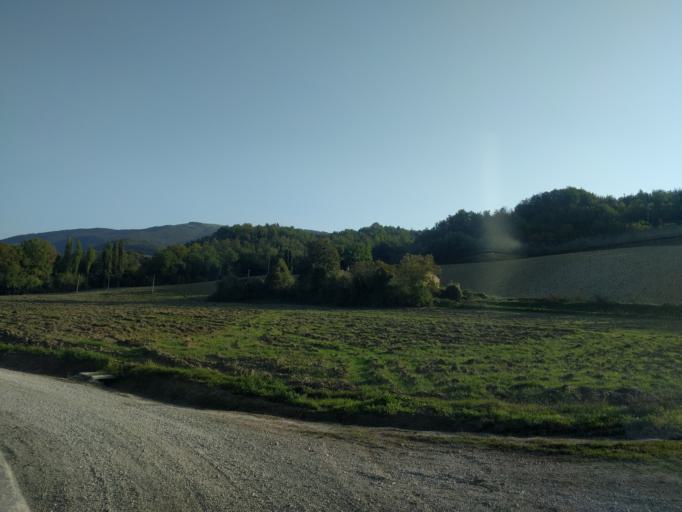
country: IT
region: The Marches
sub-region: Provincia di Pesaro e Urbino
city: Canavaccio
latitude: 43.6939
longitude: 12.6894
